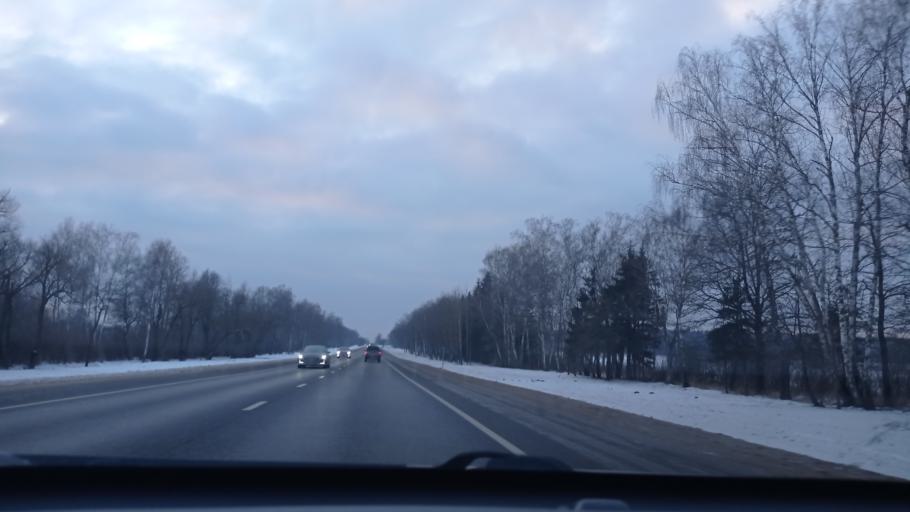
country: RU
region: Moskovskaya
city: Kievskij
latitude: 55.2295
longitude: 37.0184
